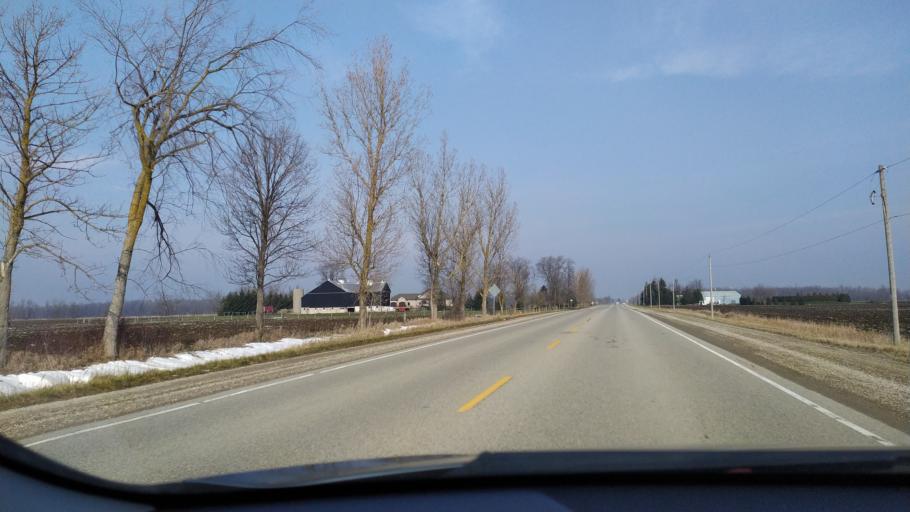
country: CA
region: Ontario
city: Stratford
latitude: 43.4855
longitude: -80.8900
